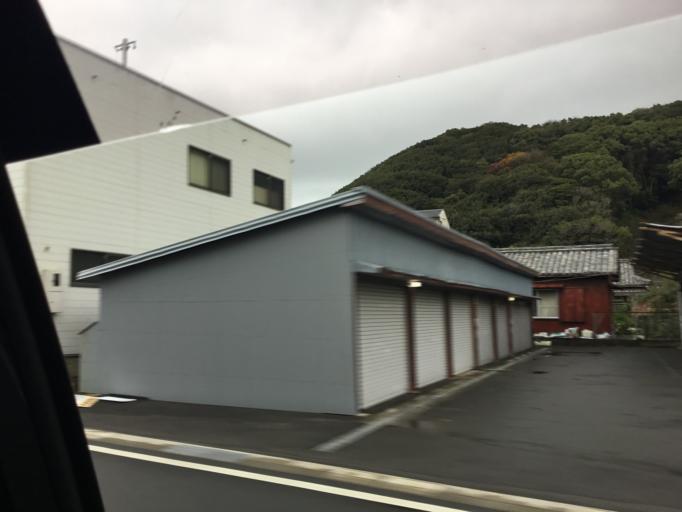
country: JP
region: Wakayama
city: Minato
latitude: 34.2755
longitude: 135.0766
